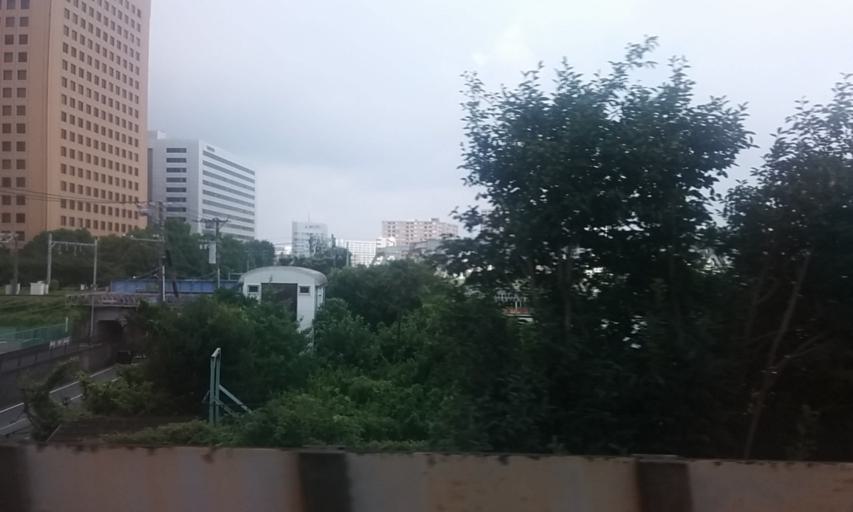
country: JP
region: Kanagawa
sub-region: Kawasaki-shi
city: Kawasaki
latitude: 35.5359
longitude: 139.7037
